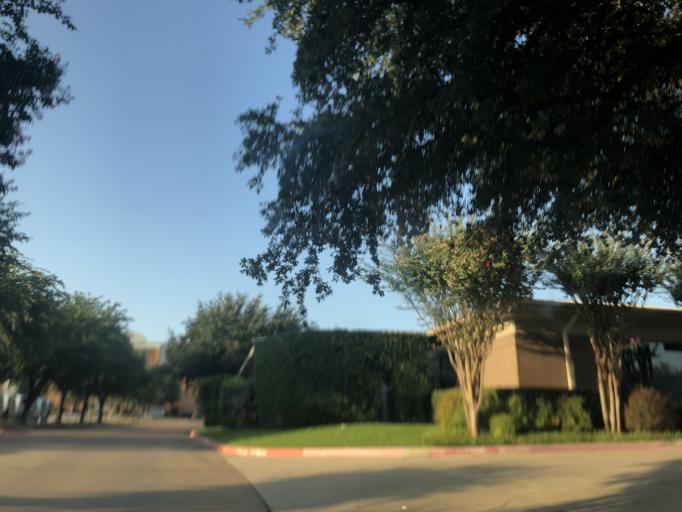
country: US
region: Texas
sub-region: Tarrant County
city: Arlington
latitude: 32.7523
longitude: -97.0662
